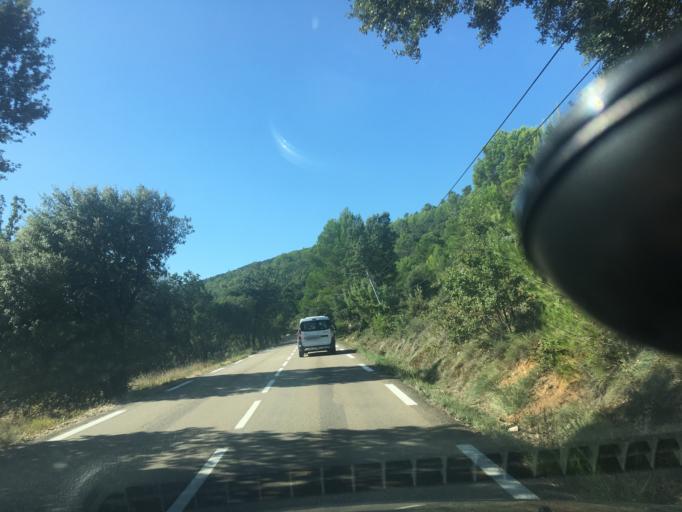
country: FR
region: Provence-Alpes-Cote d'Azur
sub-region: Departement du Var
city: Regusse
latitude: 43.6137
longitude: 6.0695
